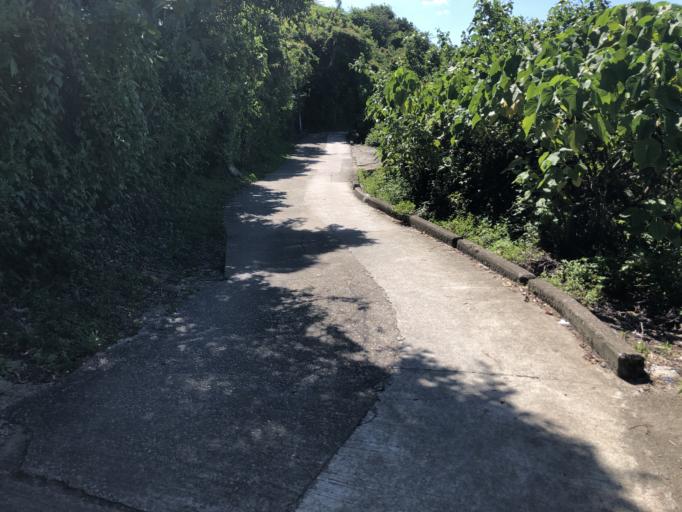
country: HK
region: Tuen Mun
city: Tuen Mun
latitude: 22.2973
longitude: 113.9688
